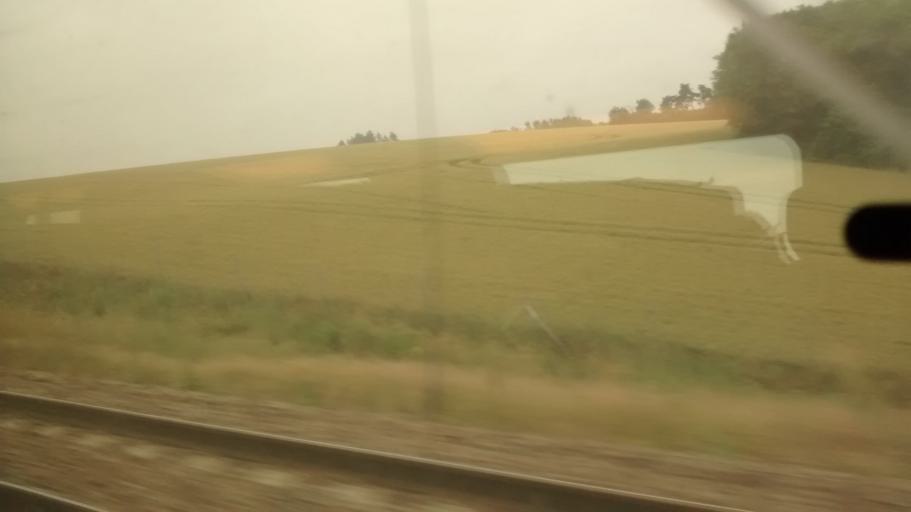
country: FR
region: Bourgogne
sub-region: Departement de l'Yonne
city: Sergines
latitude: 48.3194
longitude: 3.2344
